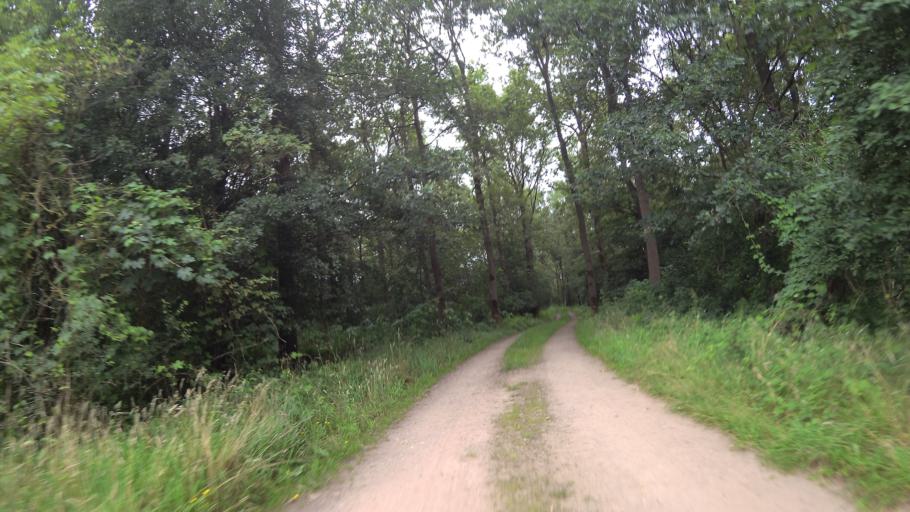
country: DE
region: Lower Saxony
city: Fresenburg
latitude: 52.8726
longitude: 7.2995
